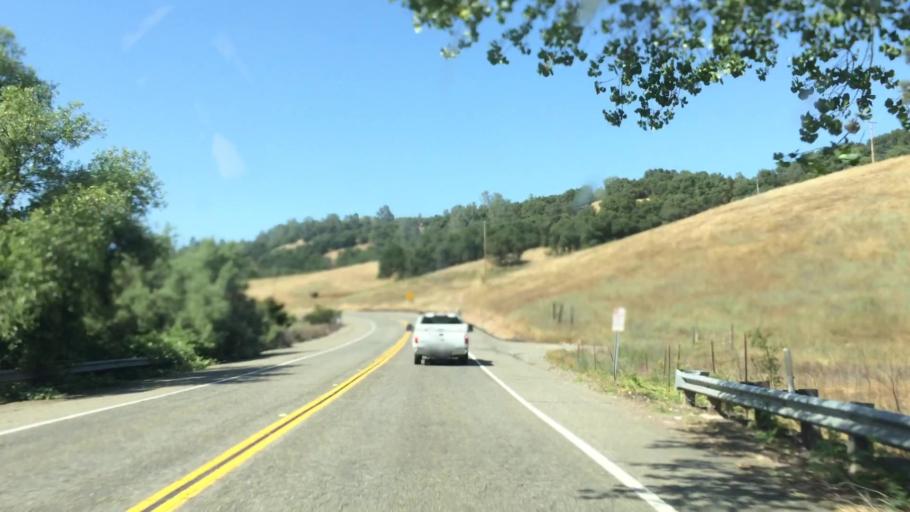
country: US
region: California
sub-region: Amador County
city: Plymouth
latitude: 38.5242
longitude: -120.9553
